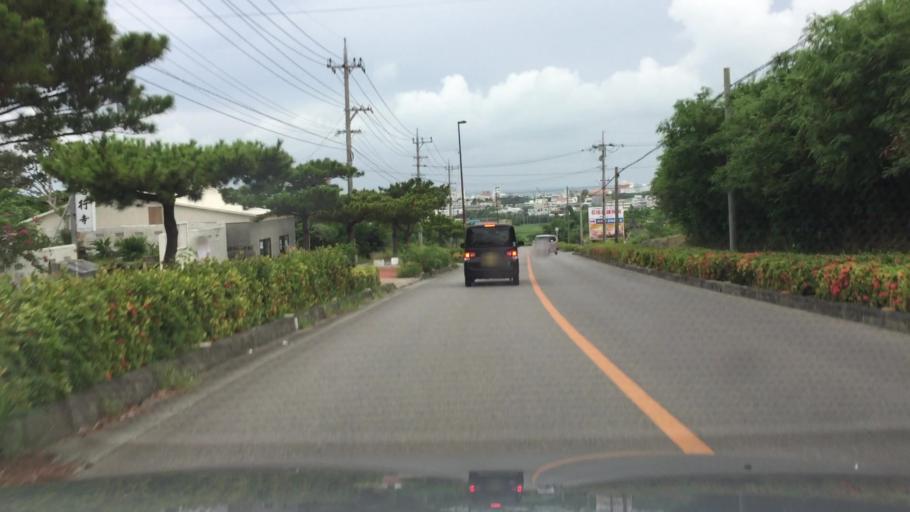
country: JP
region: Okinawa
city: Ishigaki
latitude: 24.3602
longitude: 124.1570
